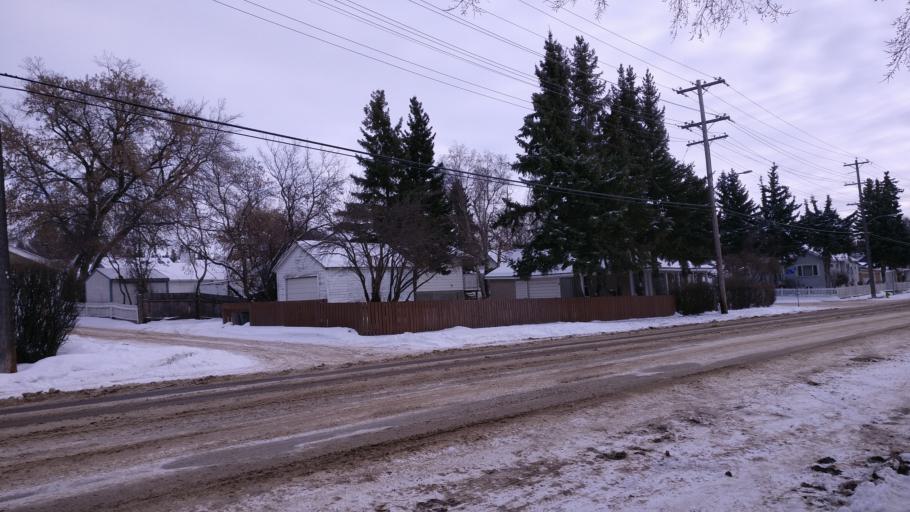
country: CA
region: Alberta
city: Red Deer
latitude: 52.2667
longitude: -113.8051
